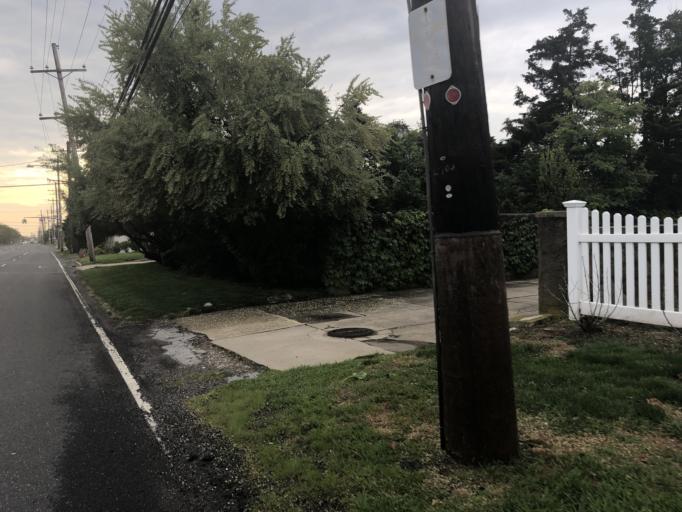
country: US
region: New York
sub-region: Nassau County
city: Atlantic Beach
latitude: 40.5891
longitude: -73.7275
